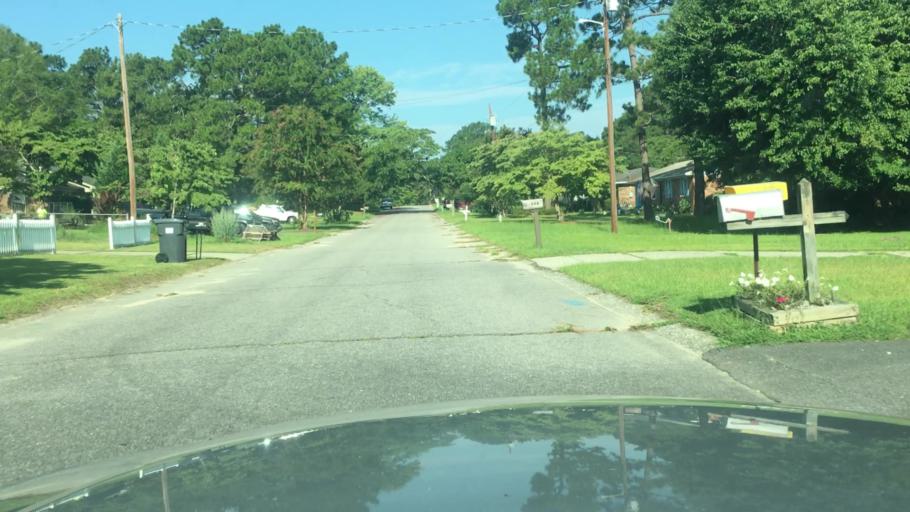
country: US
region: North Carolina
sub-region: Cumberland County
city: Spring Lake
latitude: 35.1540
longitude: -78.9204
